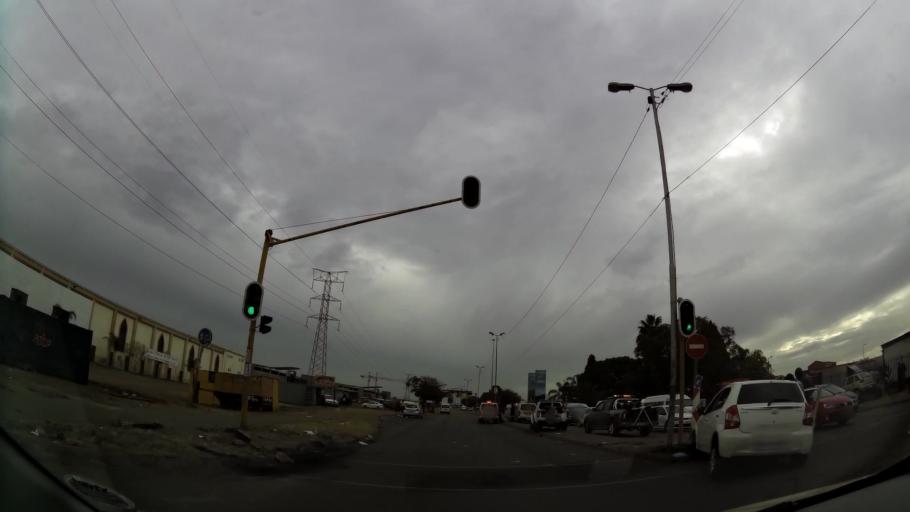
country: ZA
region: Gauteng
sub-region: City of Tshwane Metropolitan Municipality
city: Pretoria
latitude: -25.7184
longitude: 28.3448
